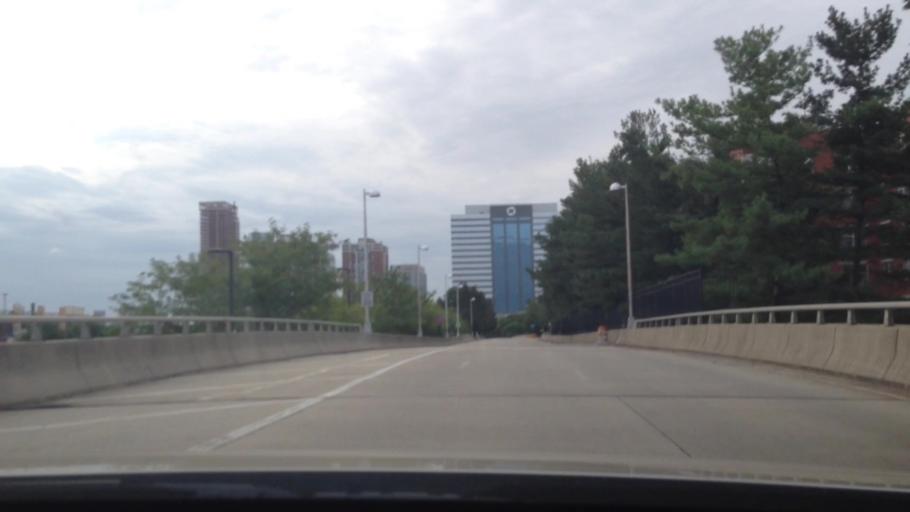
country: US
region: New Jersey
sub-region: Hudson County
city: Hoboken
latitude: 40.7295
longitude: -74.0435
